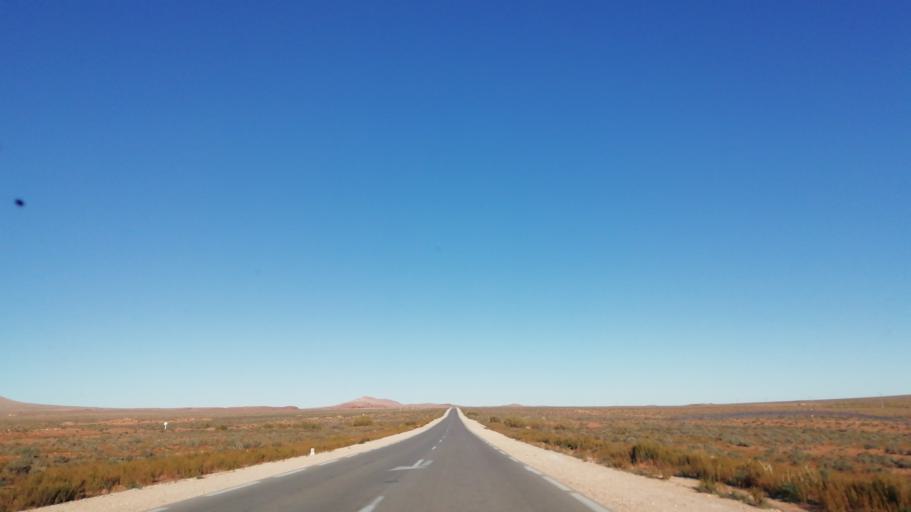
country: DZ
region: El Bayadh
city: El Abiodh Sidi Cheikh
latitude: 33.0972
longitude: 0.2047
